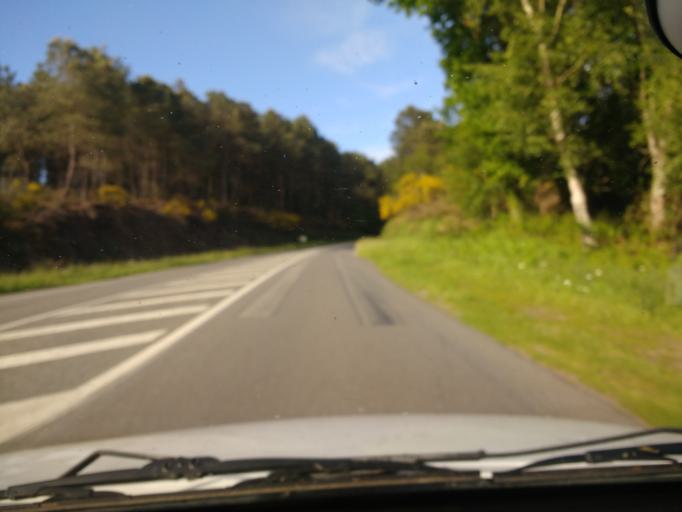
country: FR
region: Brittany
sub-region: Departement du Morbihan
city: Pluherlin
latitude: 47.7051
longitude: -2.3601
